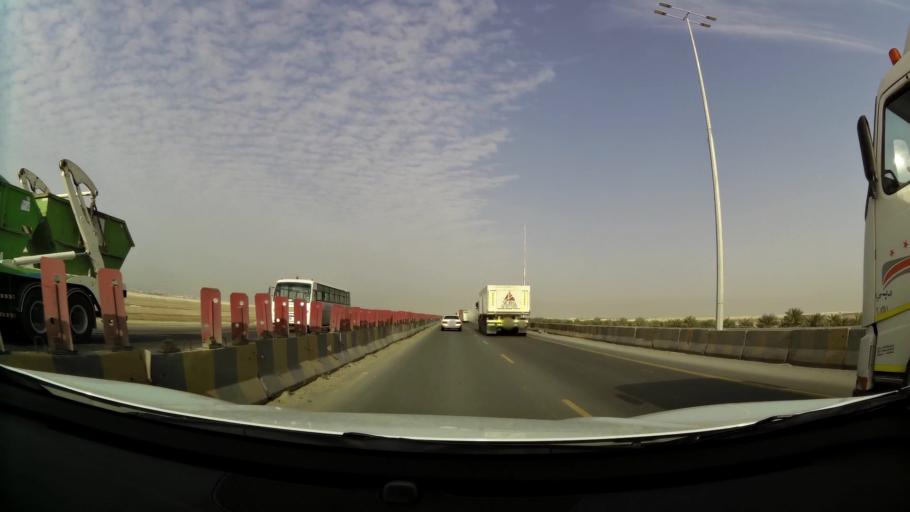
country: AE
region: Abu Dhabi
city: Abu Dhabi
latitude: 24.2261
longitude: 54.4438
